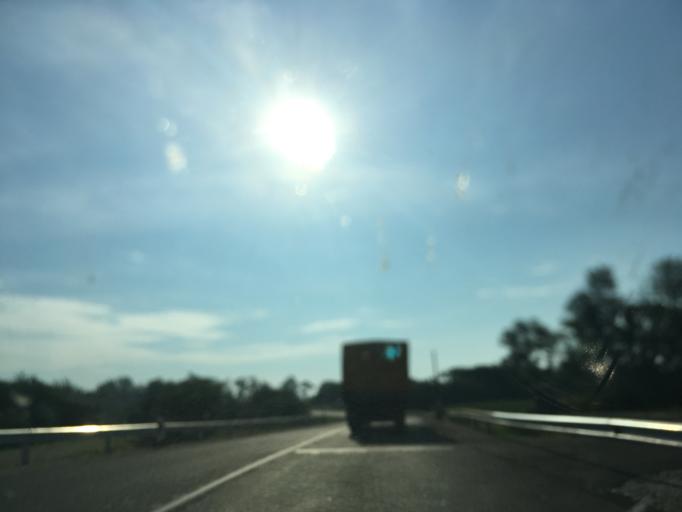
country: HU
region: Hajdu-Bihar
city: Nyiradony
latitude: 47.6818
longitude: 21.8767
